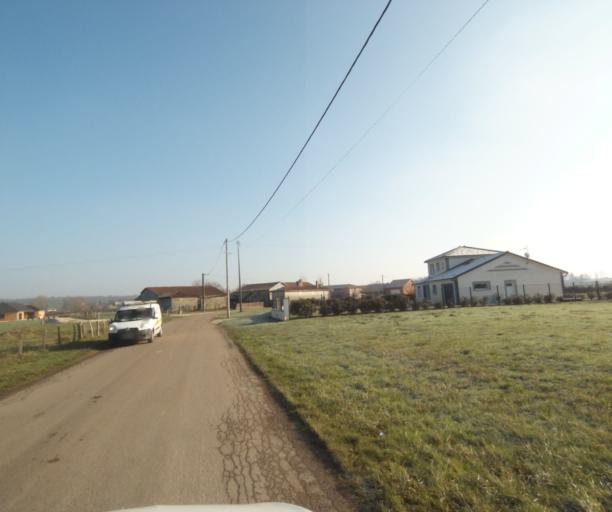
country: FR
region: Champagne-Ardenne
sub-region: Departement de la Haute-Marne
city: Montier-en-Der
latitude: 48.4785
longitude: 4.7551
